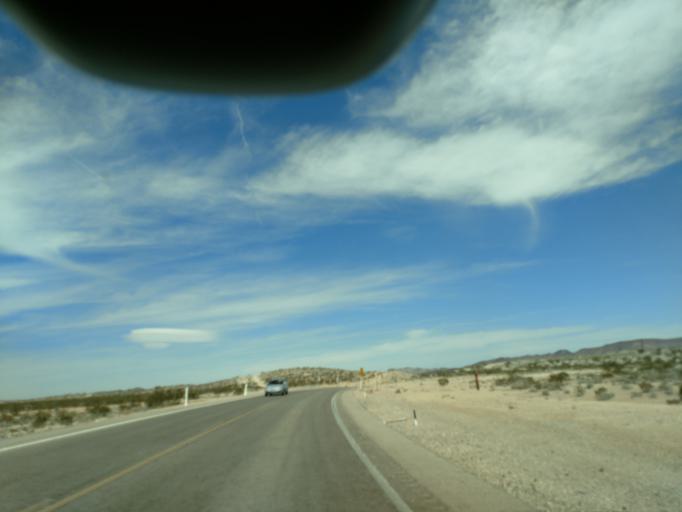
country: US
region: Nevada
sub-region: Clark County
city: Enterprise
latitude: 35.8208
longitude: -115.2935
